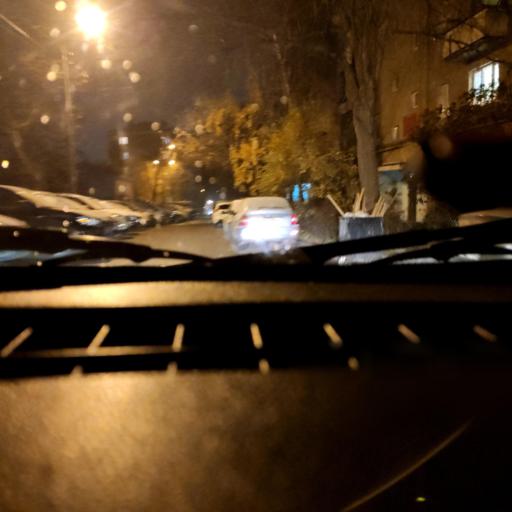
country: RU
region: Bashkortostan
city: Ufa
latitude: 54.7397
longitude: 56.0260
